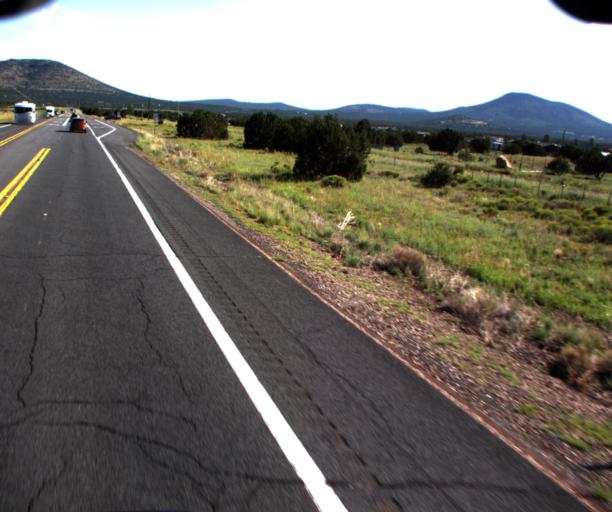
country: US
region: Arizona
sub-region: Coconino County
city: Williams
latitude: 35.3657
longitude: -112.1655
